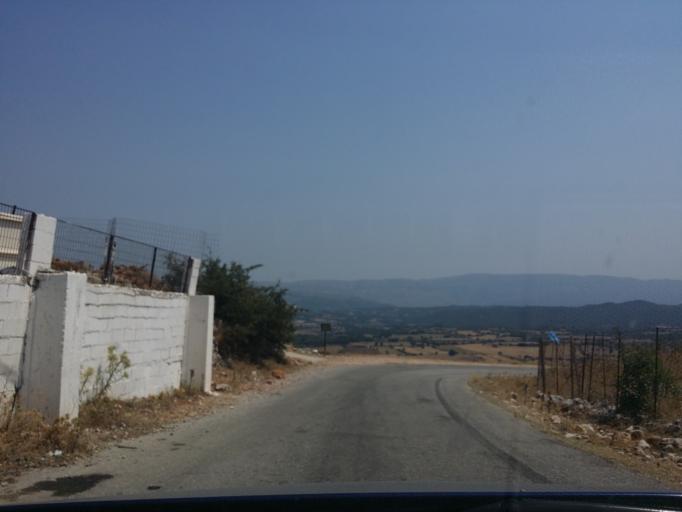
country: GR
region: West Greece
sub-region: Nomos Aitolias kai Akarnanias
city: Katouna
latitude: 38.7594
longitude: 21.0733
